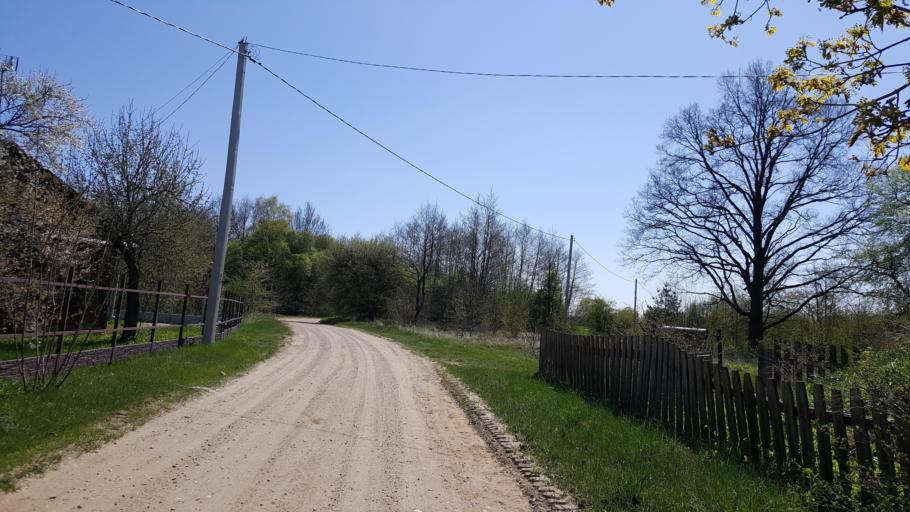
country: BY
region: Brest
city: Kamyanyets
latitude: 52.3358
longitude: 23.7473
